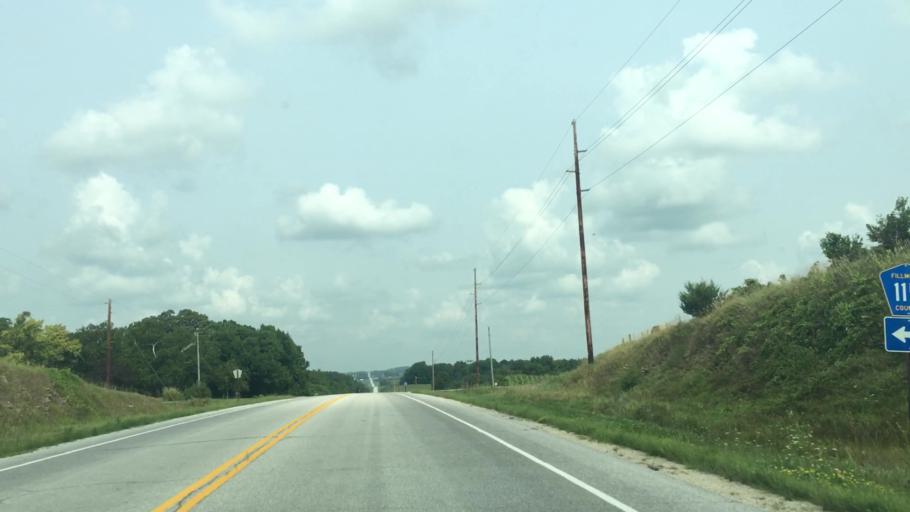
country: US
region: Minnesota
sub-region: Fillmore County
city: Harmony
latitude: 43.5794
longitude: -91.9299
